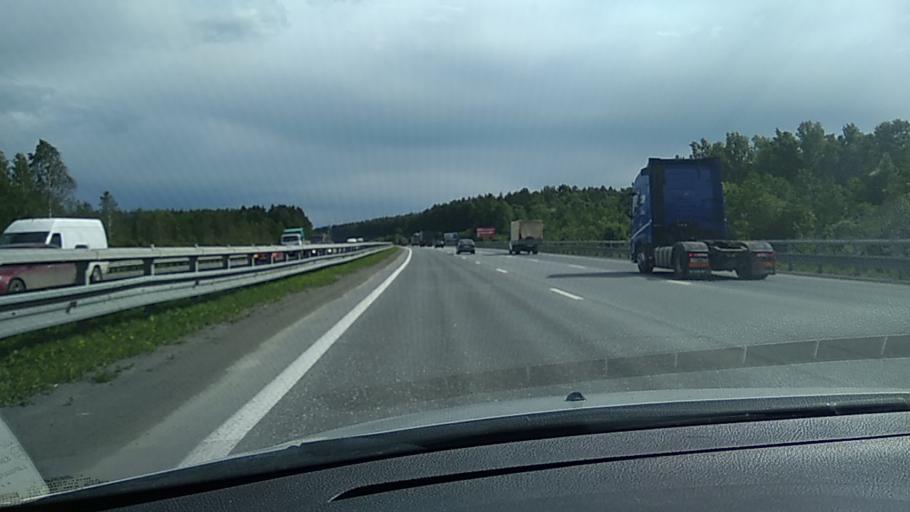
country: RU
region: Sverdlovsk
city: Shuvakish
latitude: 56.9170
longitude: 60.5080
